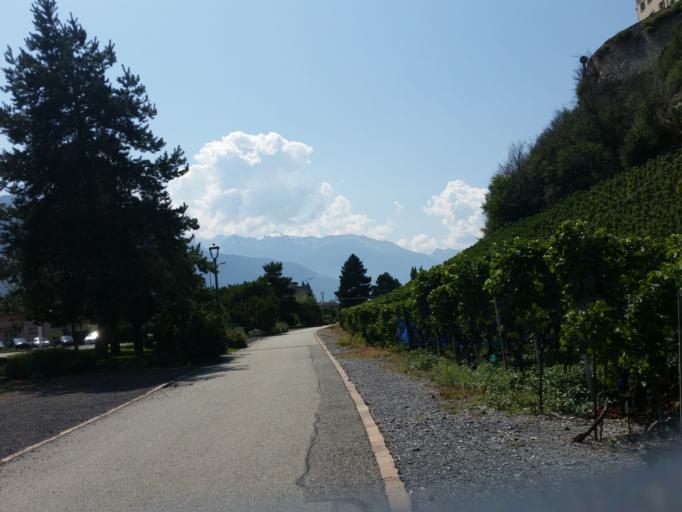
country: CH
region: Valais
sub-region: Martigny District
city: Saillon
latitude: 46.1716
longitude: 7.1867
